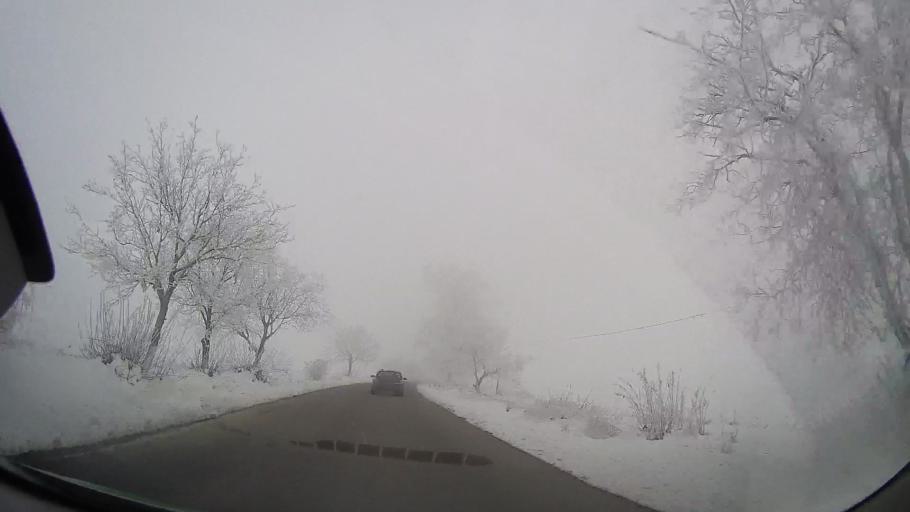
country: RO
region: Neamt
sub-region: Comuna Sabaoani
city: Sabaoani
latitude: 46.9897
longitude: 26.8629
